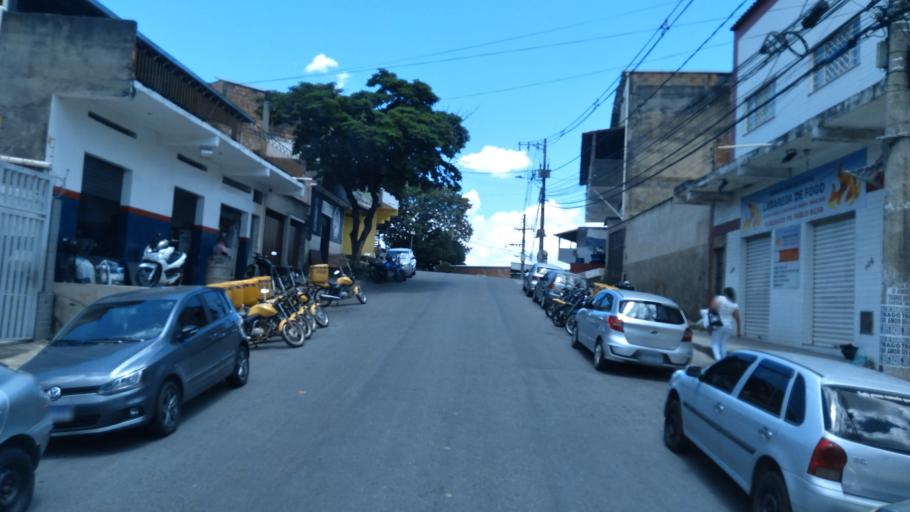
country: BR
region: Minas Gerais
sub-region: Belo Horizonte
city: Belo Horizonte
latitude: -19.8460
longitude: -43.8967
